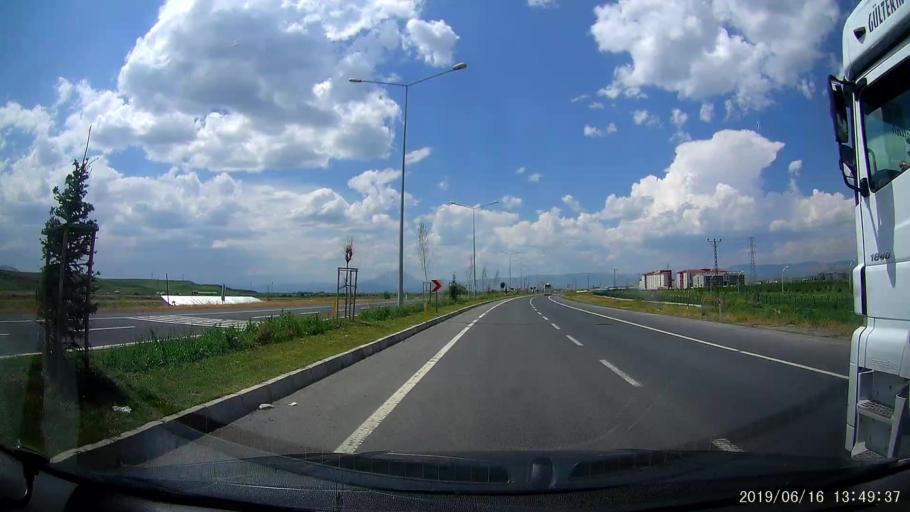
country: TR
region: Agri
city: Agri
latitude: 39.7187
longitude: 42.9884
